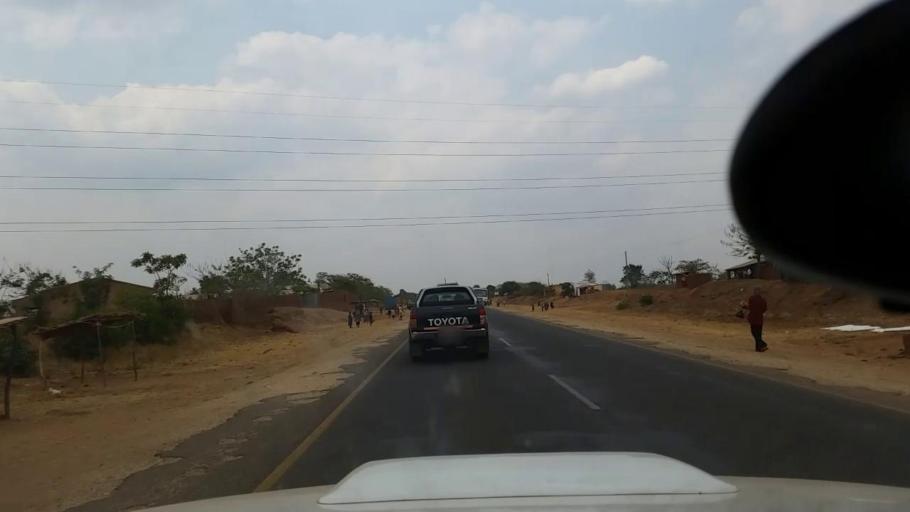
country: MW
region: Central Region
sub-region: Lilongwe District
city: Lilongwe
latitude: -13.8654
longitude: 33.8295
